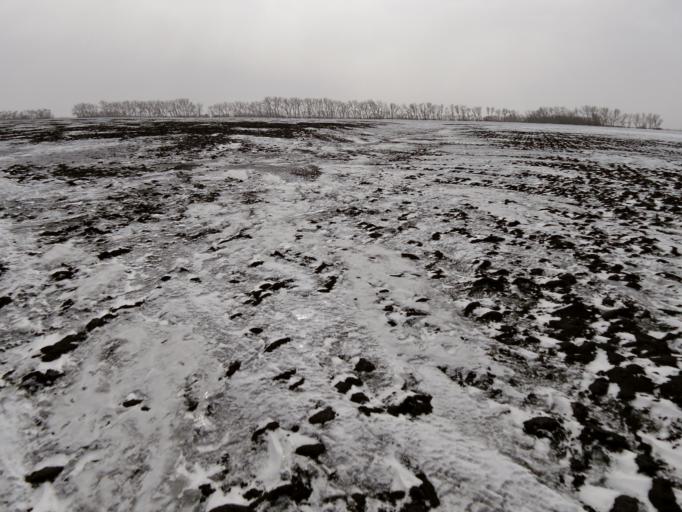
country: US
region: North Dakota
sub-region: Walsh County
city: Grafton
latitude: 48.3994
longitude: -97.2078
